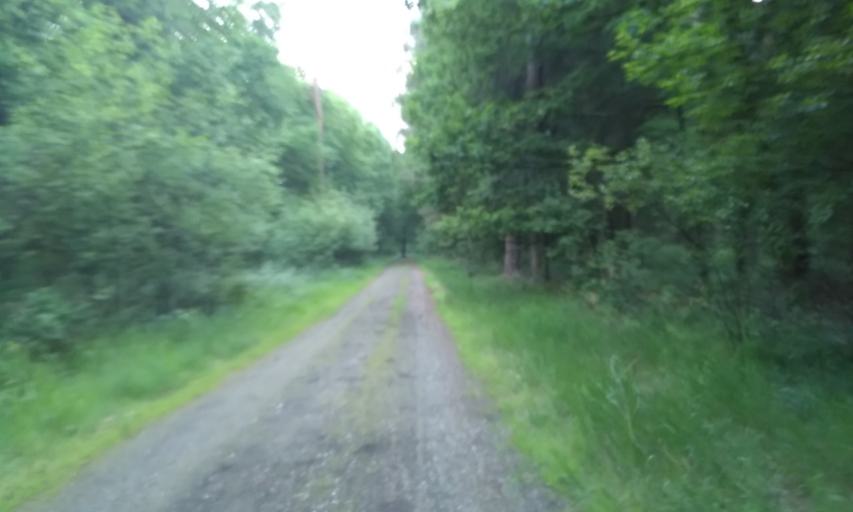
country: DE
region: Lower Saxony
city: Dollern
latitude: 53.5247
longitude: 9.5115
